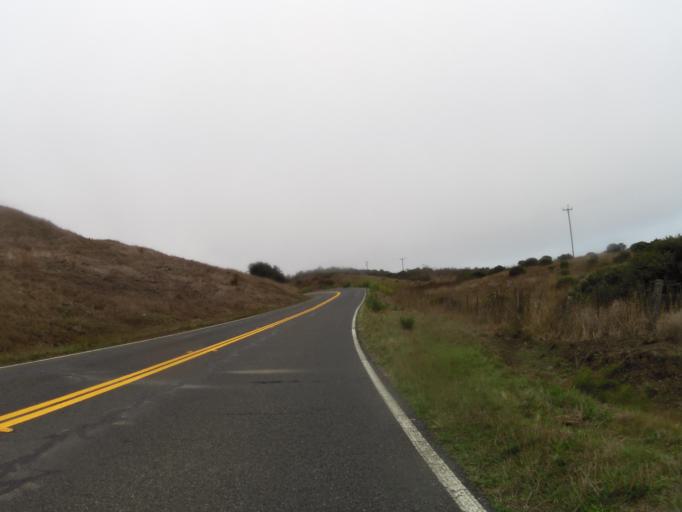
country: US
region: California
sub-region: Sonoma County
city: Monte Rio
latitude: 38.5075
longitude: -123.2265
